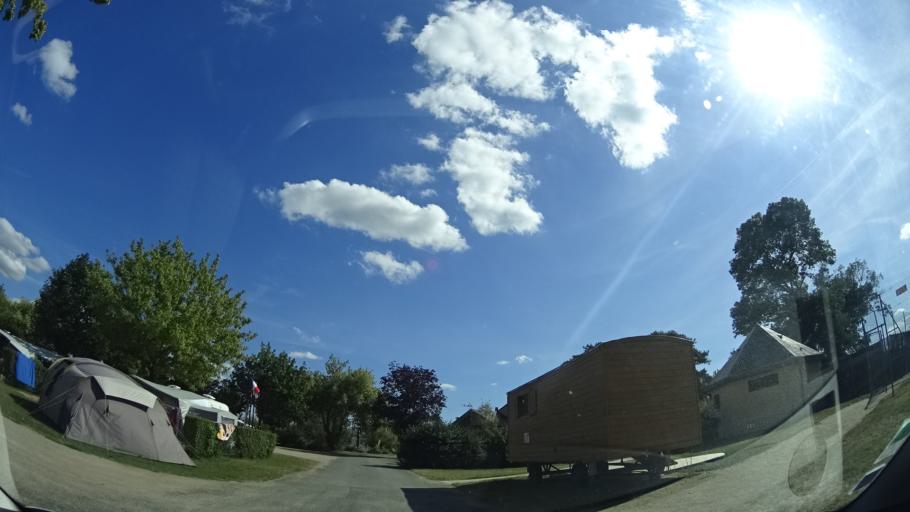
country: FR
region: Pays de la Loire
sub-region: Departement de la Sarthe
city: La Fleche
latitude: 47.6958
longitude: -0.0793
